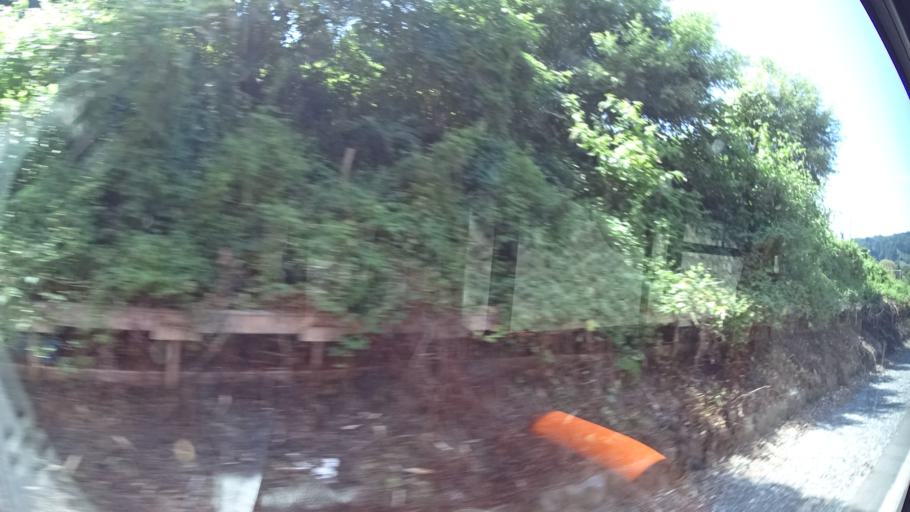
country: JP
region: Iwate
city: Ofunato
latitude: 38.9887
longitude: 141.7114
